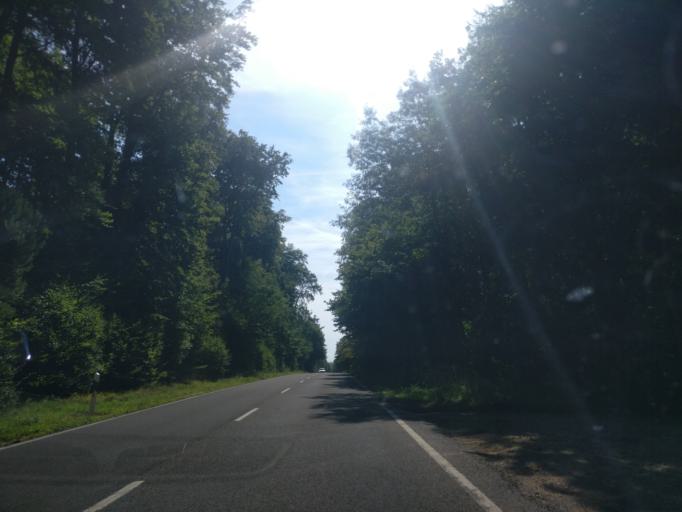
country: LU
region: Luxembourg
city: Bereldange
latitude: 49.6407
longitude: 6.1050
